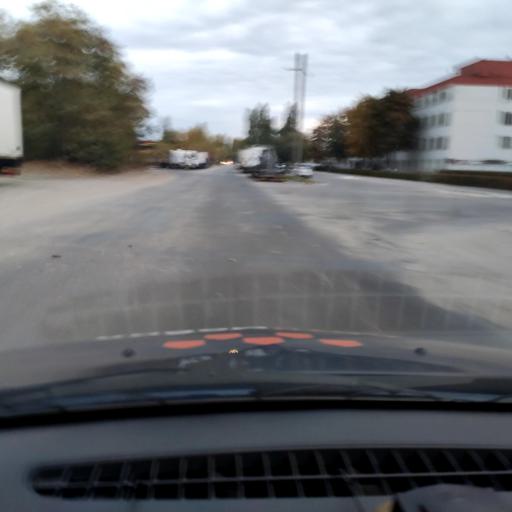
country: RU
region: Voronezj
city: Pridonskoy
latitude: 51.6764
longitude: 39.0923
